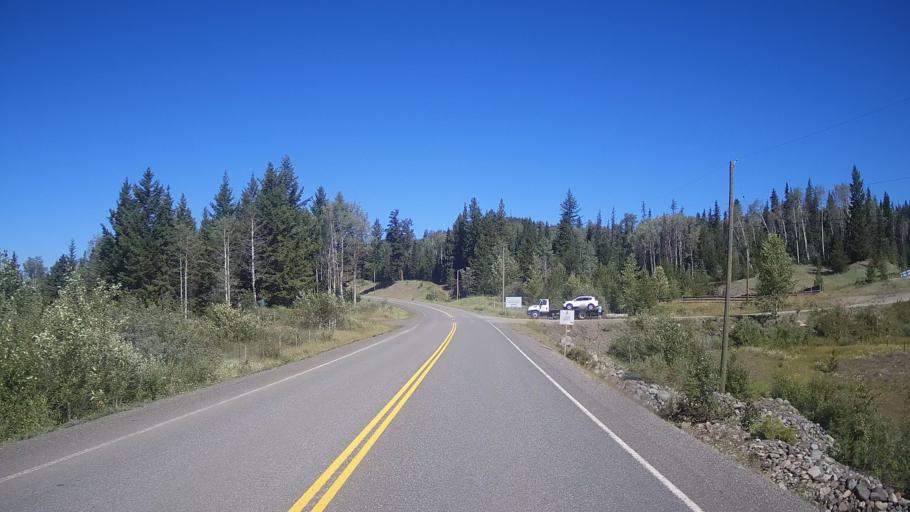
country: CA
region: British Columbia
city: Kamloops
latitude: 51.4913
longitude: -120.5674
